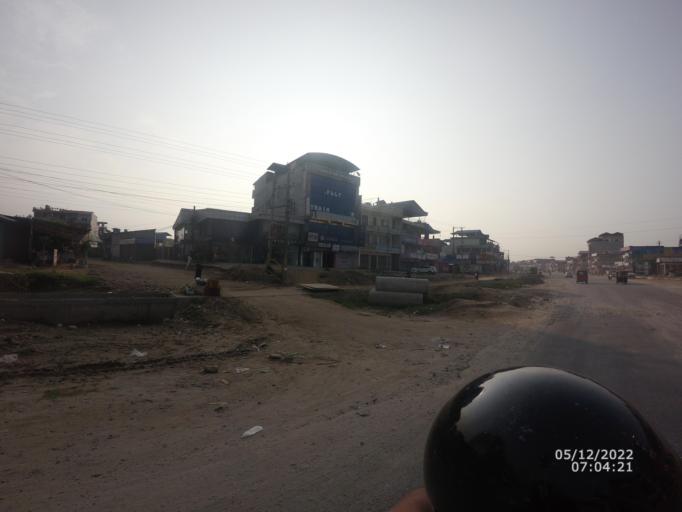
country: NP
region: Central Region
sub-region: Narayani Zone
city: Bharatpur
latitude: 27.6723
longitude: 84.4334
